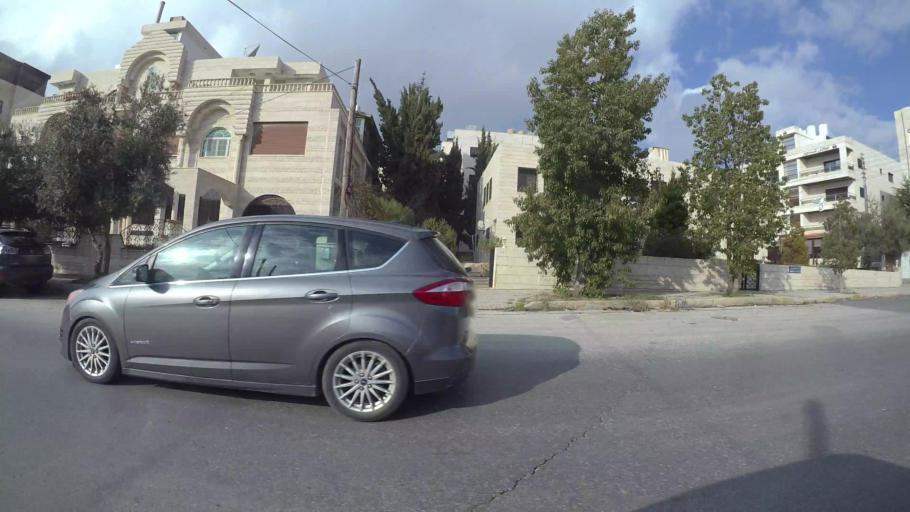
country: JO
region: Amman
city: Wadi as Sir
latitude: 31.9814
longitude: 35.8450
